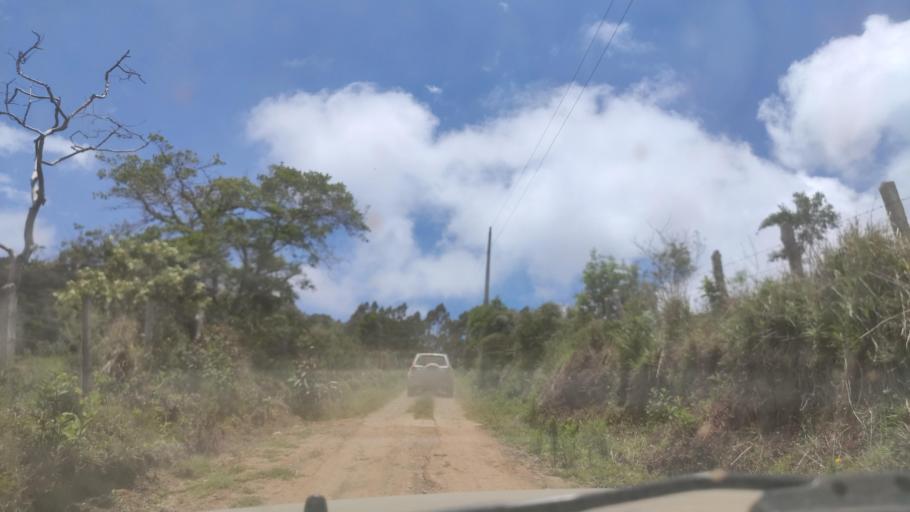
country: BR
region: Minas Gerais
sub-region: Cambui
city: Cambui
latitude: -22.6850
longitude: -45.9580
